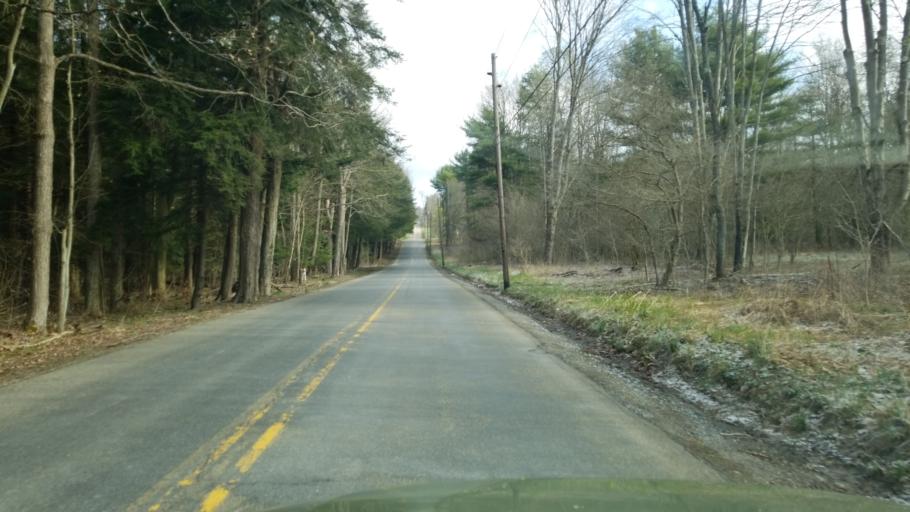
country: US
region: Pennsylvania
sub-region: Jefferson County
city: Brockway
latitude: 41.2553
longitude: -78.8384
